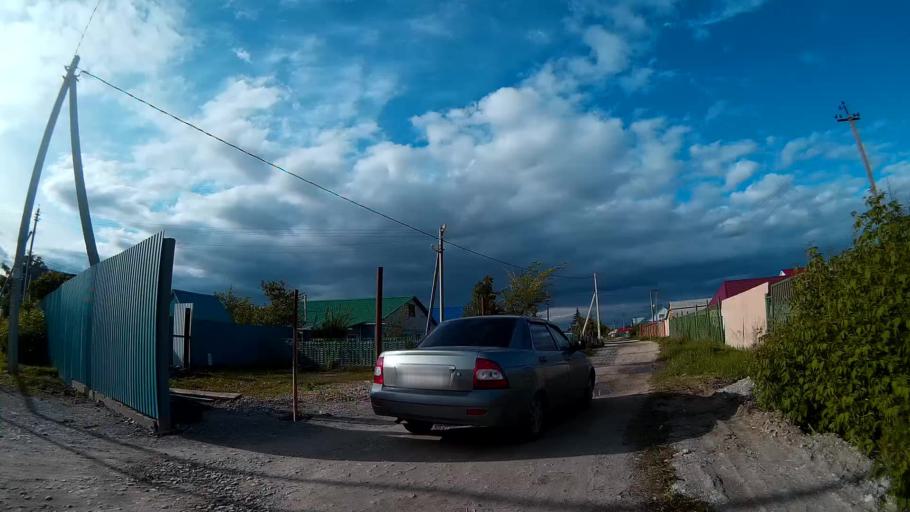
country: RU
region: Ulyanovsk
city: Novoul'yanovsk
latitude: 54.2008
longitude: 48.2693
